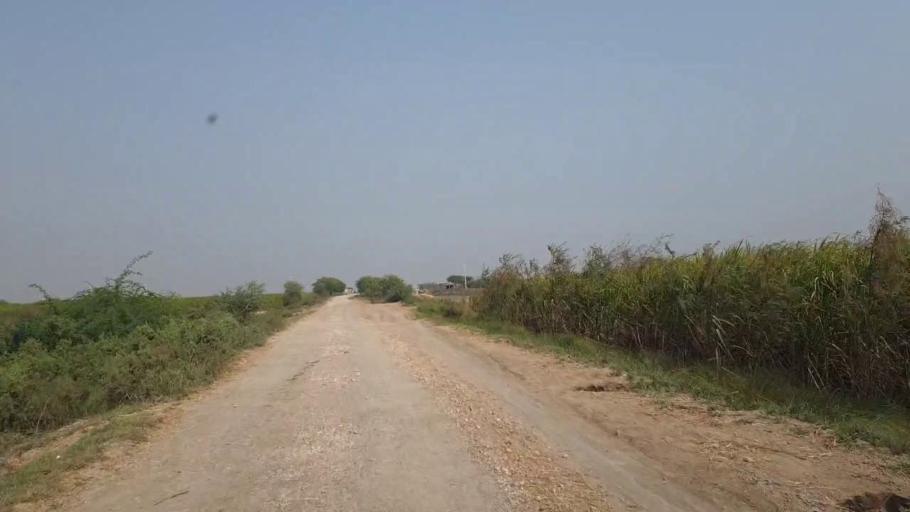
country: PK
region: Sindh
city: Kario
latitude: 24.9112
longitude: 68.6012
